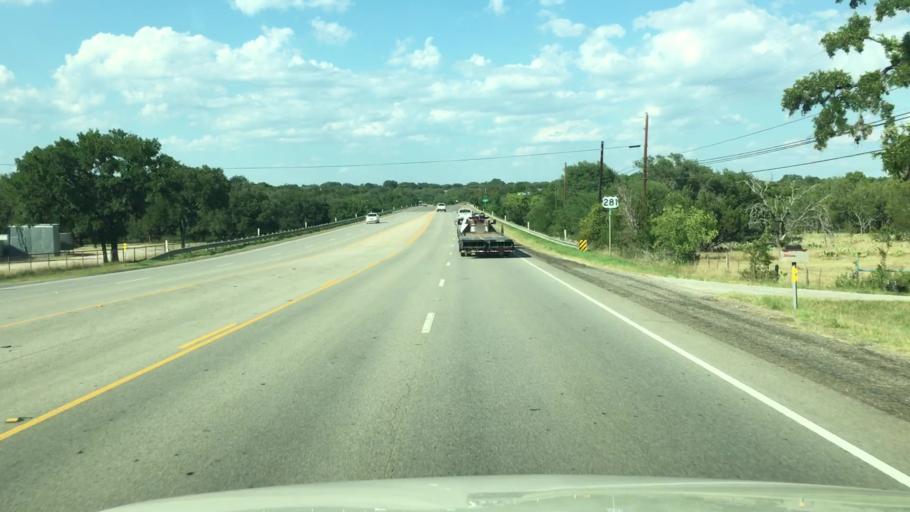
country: US
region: Texas
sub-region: Blanco County
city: Johnson City
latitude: 30.2894
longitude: -98.4027
